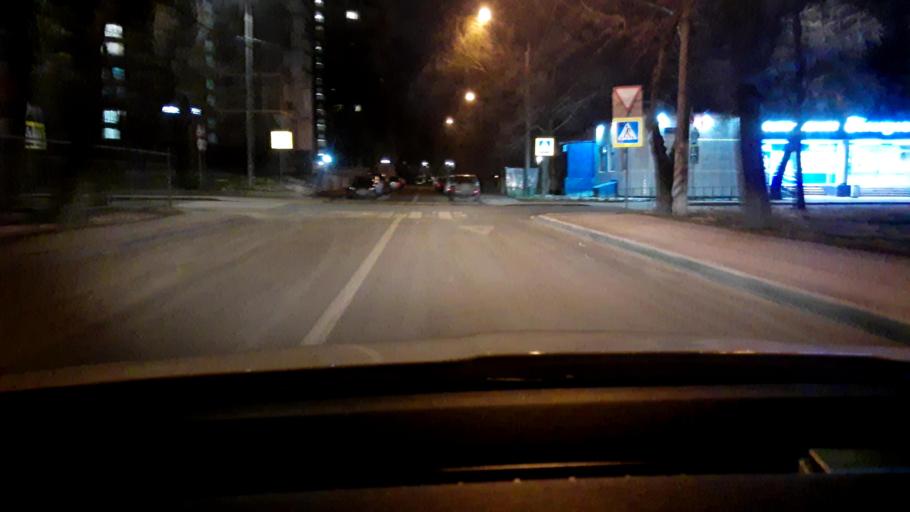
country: RU
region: Moscow
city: Leonovo
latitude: 55.8603
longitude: 37.6422
